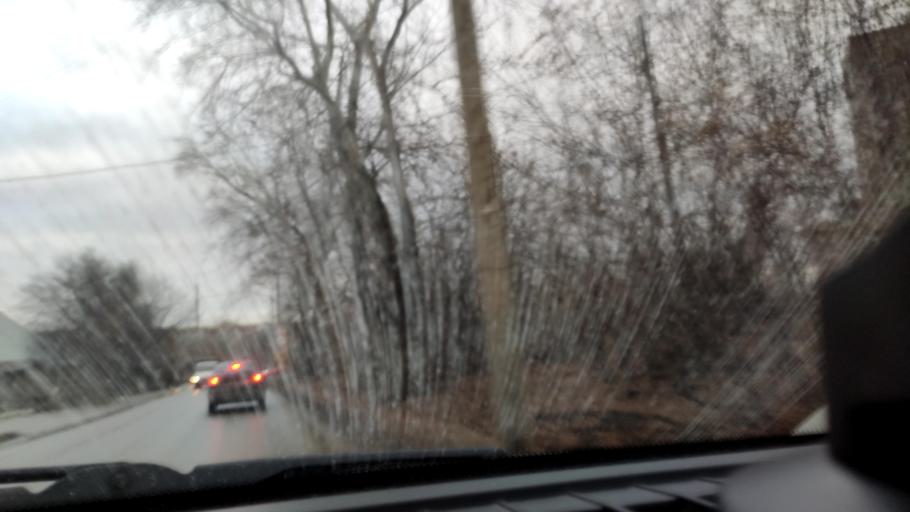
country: RU
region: Perm
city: Perm
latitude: 57.9739
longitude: 56.1940
